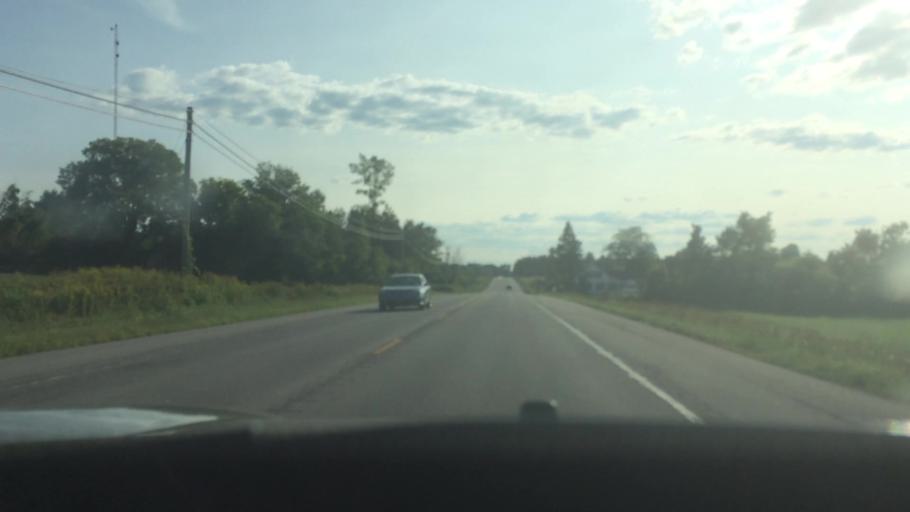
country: US
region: New York
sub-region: St. Lawrence County
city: Potsdam
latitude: 44.6459
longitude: -75.0561
